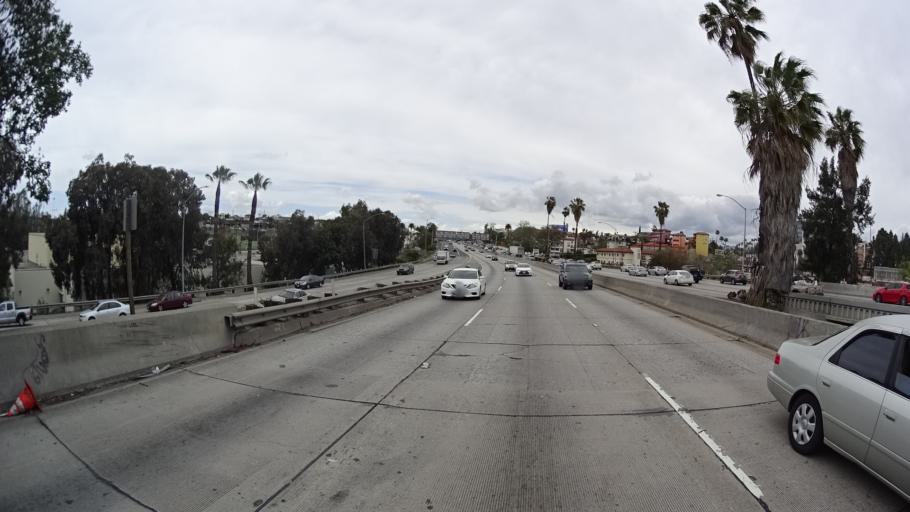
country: US
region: California
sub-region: Los Angeles County
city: Los Angeles
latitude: 34.0633
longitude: -118.2495
